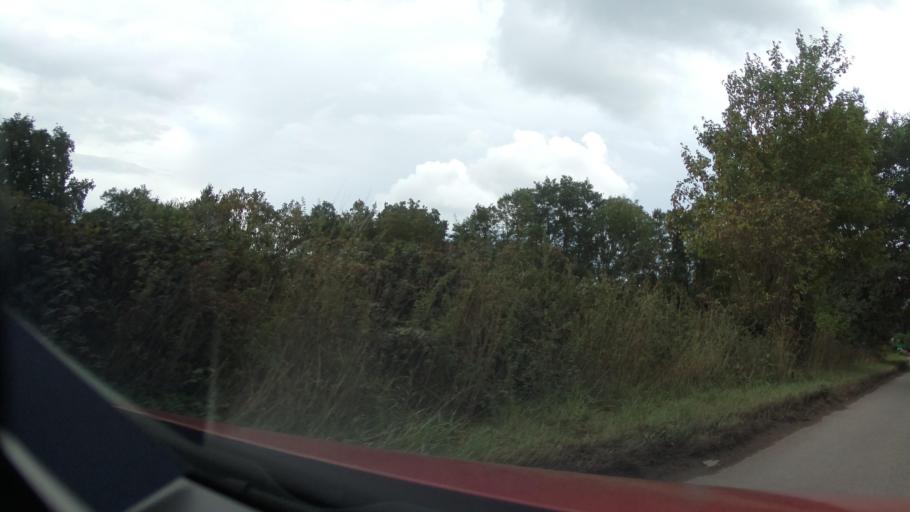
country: GB
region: England
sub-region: Staffordshire
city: Eccleshall
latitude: 52.8942
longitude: -2.2156
